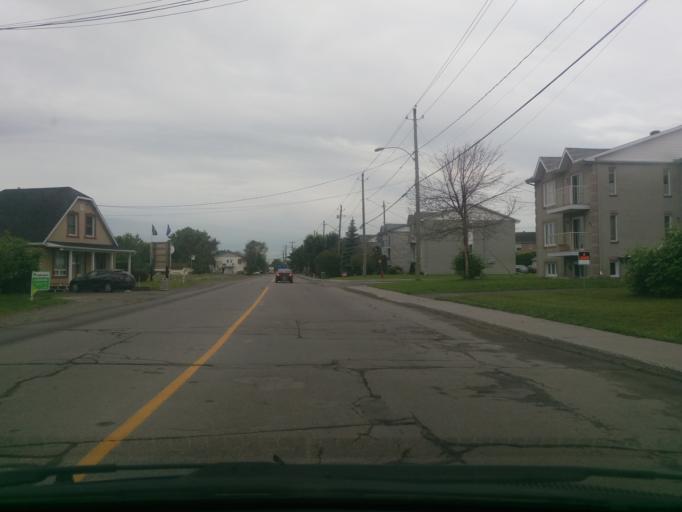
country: CA
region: Quebec
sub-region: Outaouais
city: Gatineau
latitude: 45.4723
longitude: -75.6773
